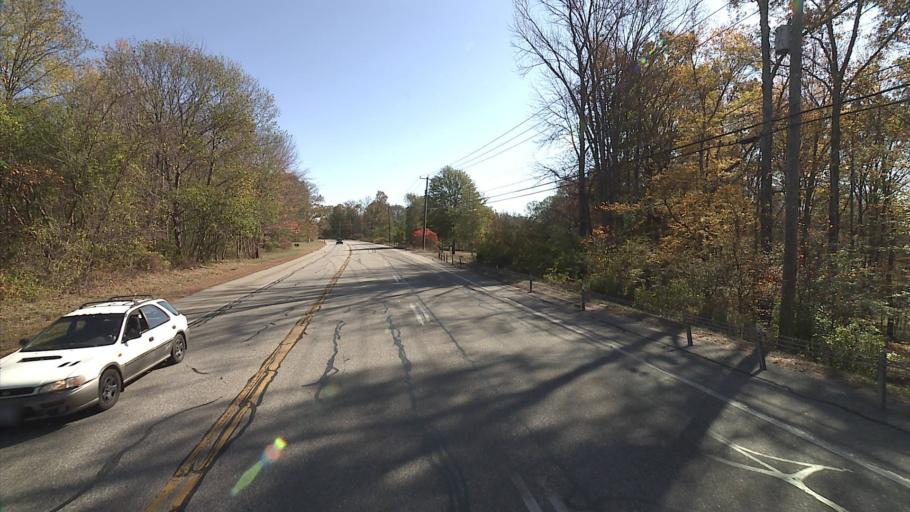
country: US
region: Connecticut
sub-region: Windham County
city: Windham
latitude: 41.7680
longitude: -72.1182
